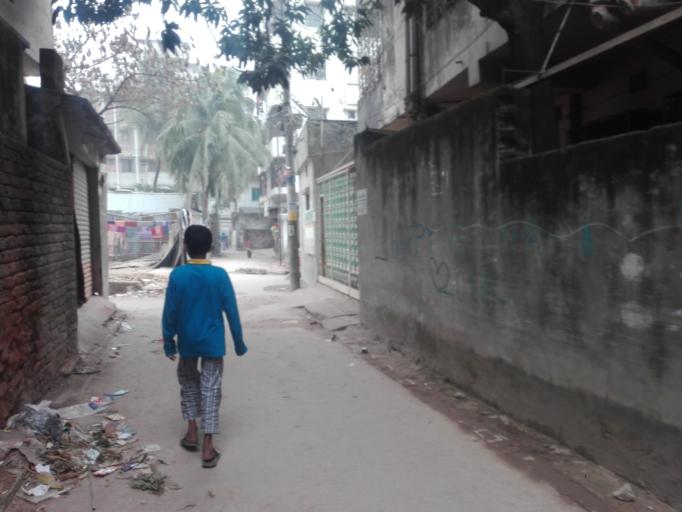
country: BD
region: Dhaka
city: Azimpur
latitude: 23.7927
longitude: 90.3598
